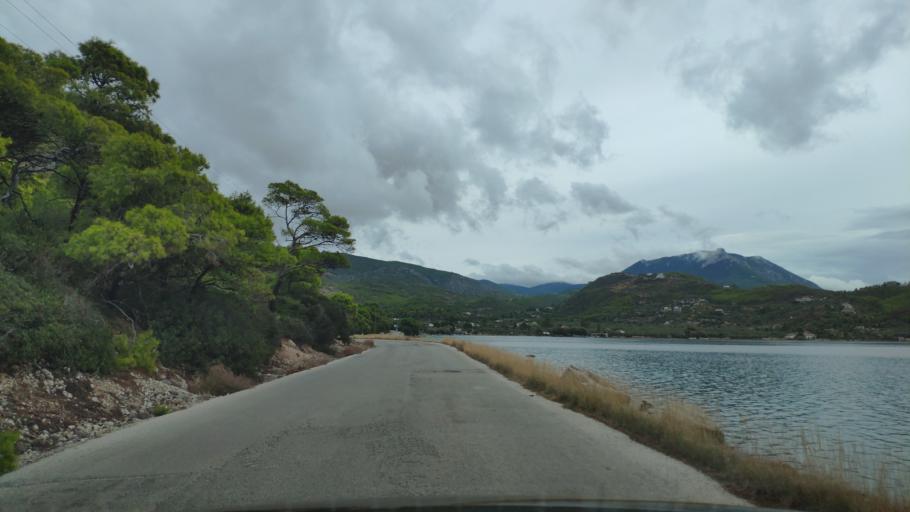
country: GR
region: Peloponnese
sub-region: Nomos Korinthias
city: Perachora
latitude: 38.0324
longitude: 22.8853
